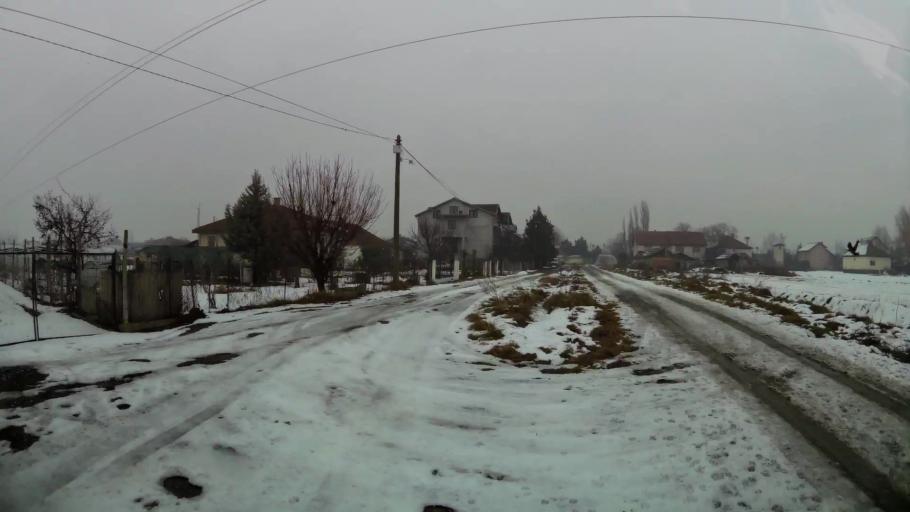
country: MK
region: Petrovec
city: Petrovec
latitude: 41.9245
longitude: 21.6290
